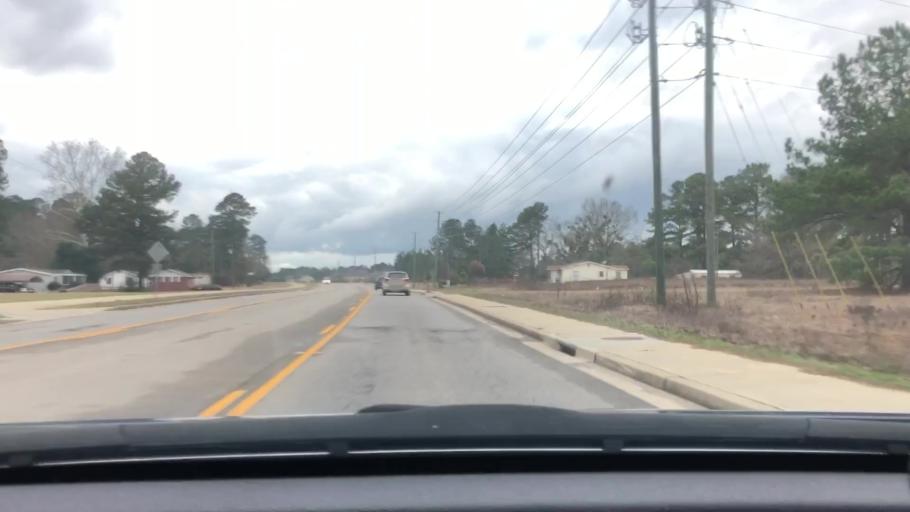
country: US
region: South Carolina
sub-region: Sumter County
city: Cane Savannah
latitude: 33.9272
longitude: -80.4081
